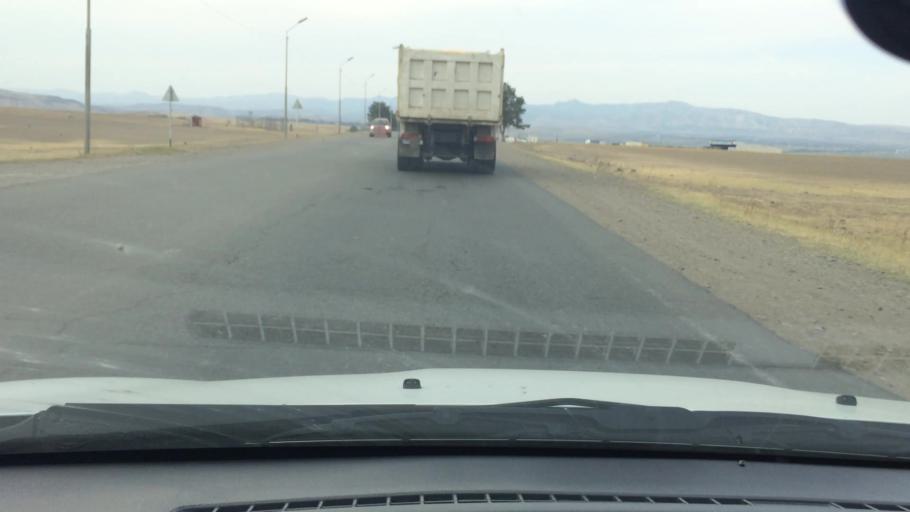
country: GE
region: Kvemo Kartli
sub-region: Marneuli
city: Marneuli
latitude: 41.5105
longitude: 44.7921
